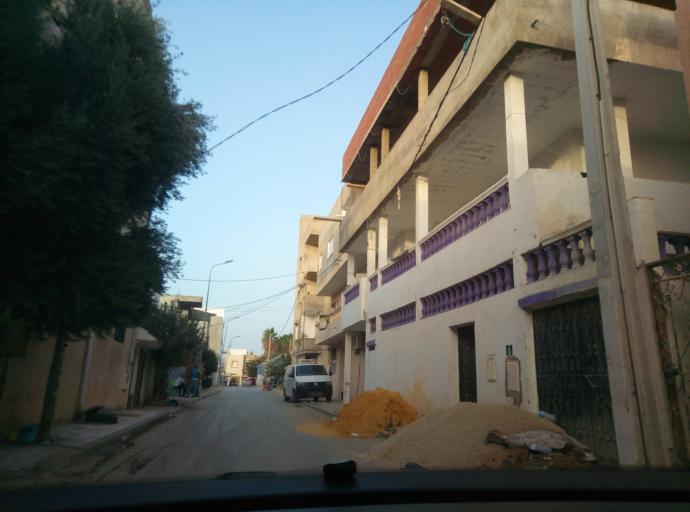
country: TN
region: Tunis
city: La Goulette
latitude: 36.8541
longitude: 10.2673
